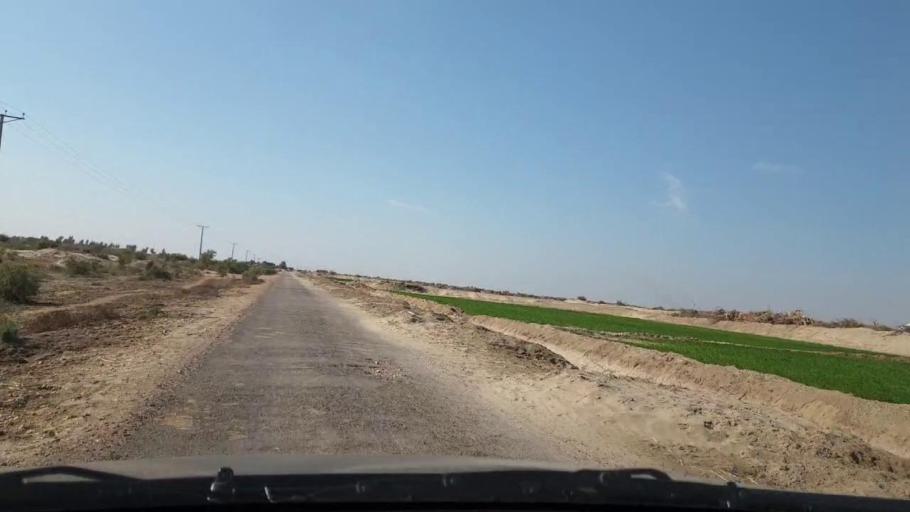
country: PK
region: Sindh
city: Khadro
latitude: 26.2694
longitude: 68.7917
